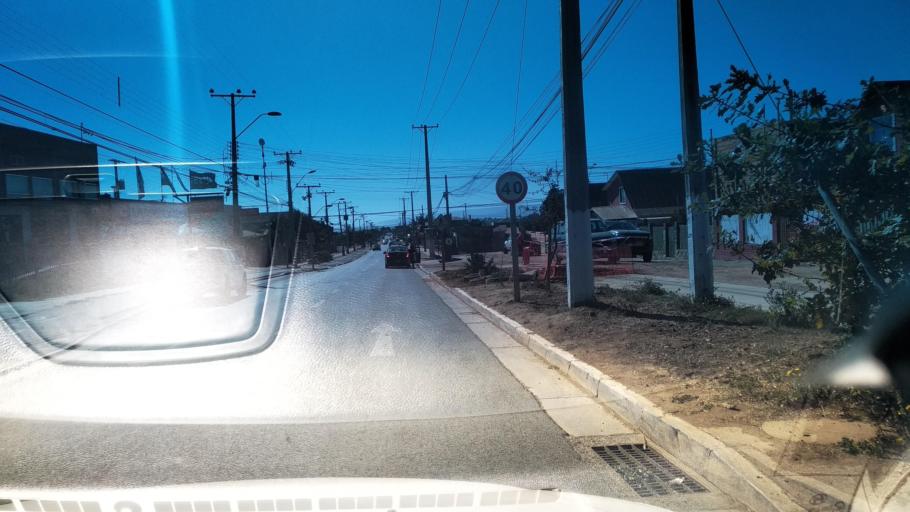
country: CL
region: O'Higgins
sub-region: Provincia de Colchagua
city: Santa Cruz
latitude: -34.3979
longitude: -71.9956
